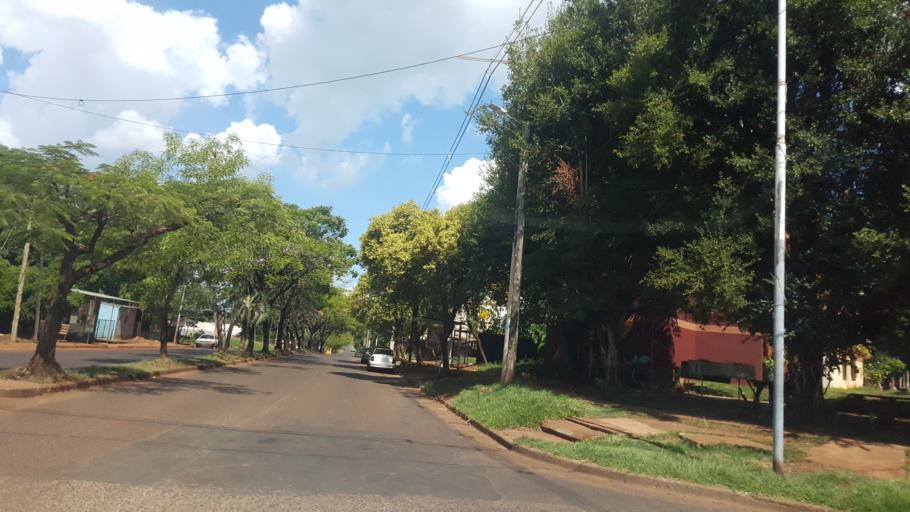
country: AR
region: Misiones
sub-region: Departamento de Capital
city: Posadas
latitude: -27.3573
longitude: -55.9303
